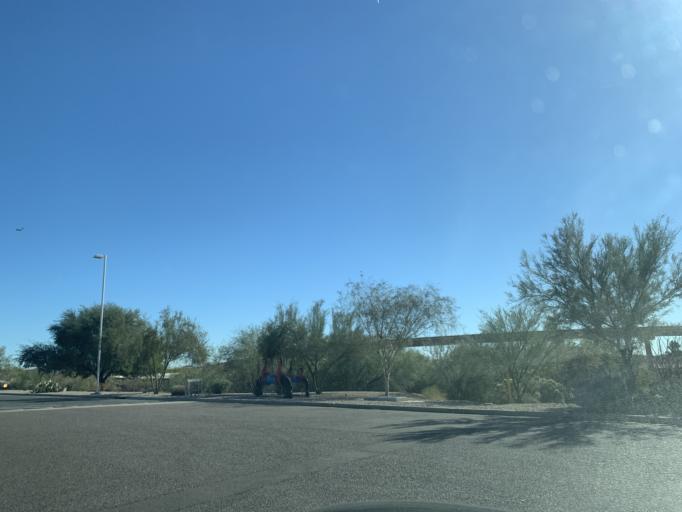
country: US
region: Arizona
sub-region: Maricopa County
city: Tempe Junction
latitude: 33.4406
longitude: -111.9784
